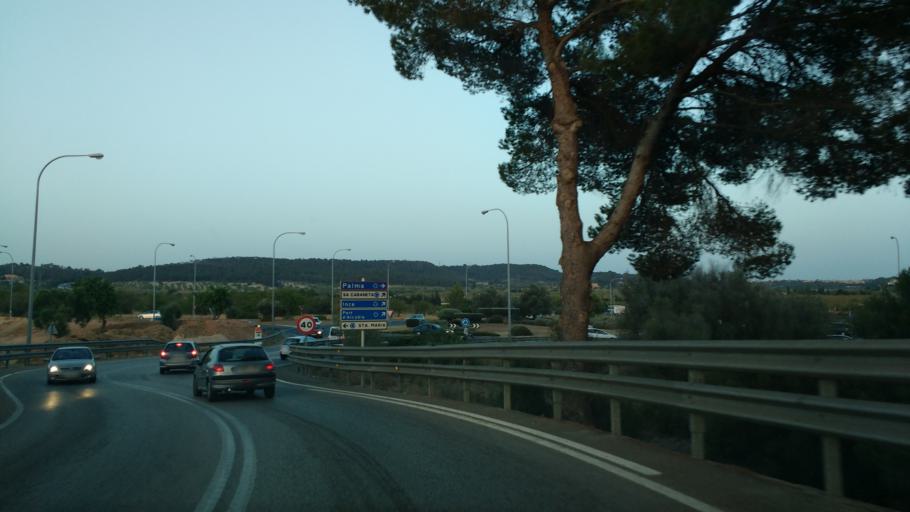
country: ES
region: Balearic Islands
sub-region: Illes Balears
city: Marratxi
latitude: 39.6315
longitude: 2.7363
